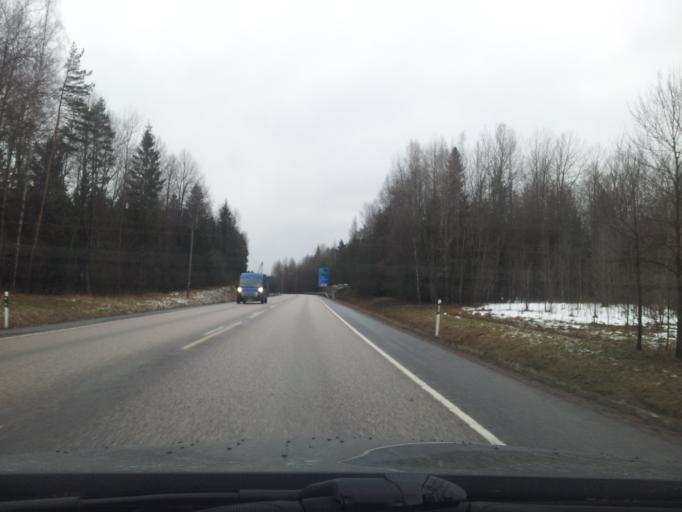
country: FI
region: Uusimaa
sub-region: Helsinki
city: Kirkkonummi
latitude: 60.1461
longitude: 24.5393
